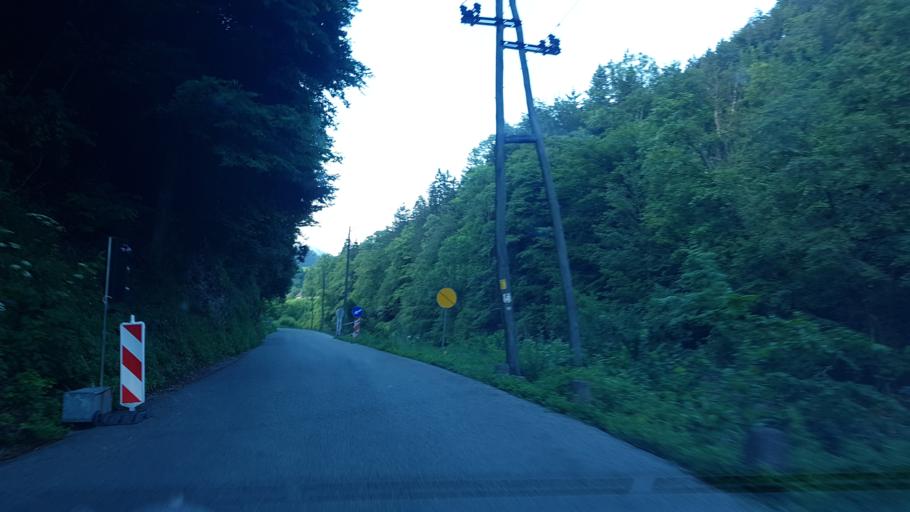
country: SI
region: Ziri
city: Ziri
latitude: 46.0885
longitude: 14.0960
